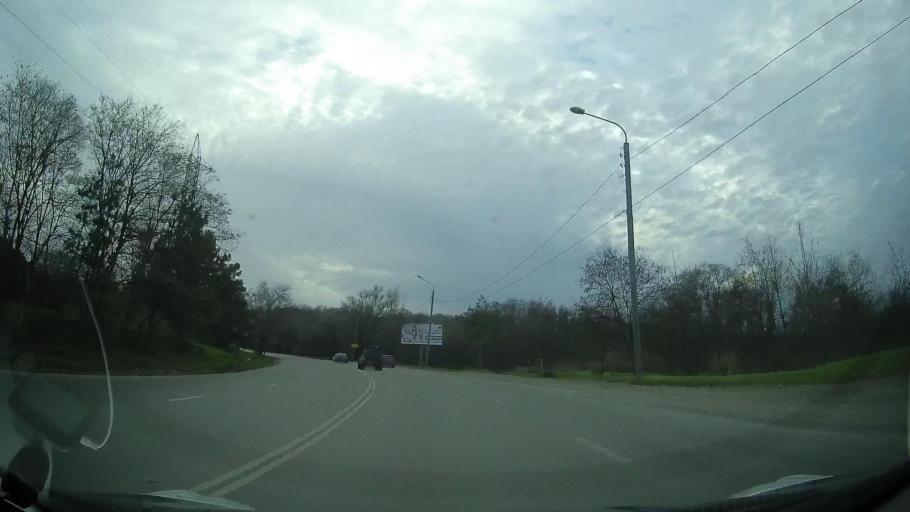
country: RU
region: Rostov
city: Aksay
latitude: 47.2480
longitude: 39.8443
